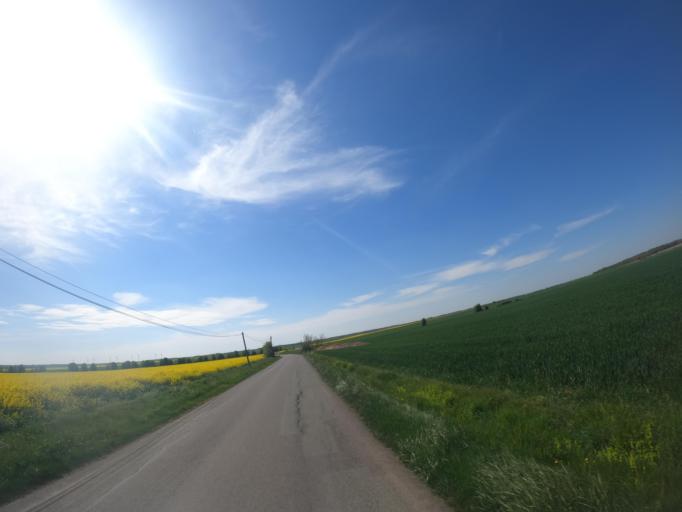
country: FR
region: Poitou-Charentes
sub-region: Departement des Deux-Sevres
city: Airvault
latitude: 46.8886
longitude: -0.1602
